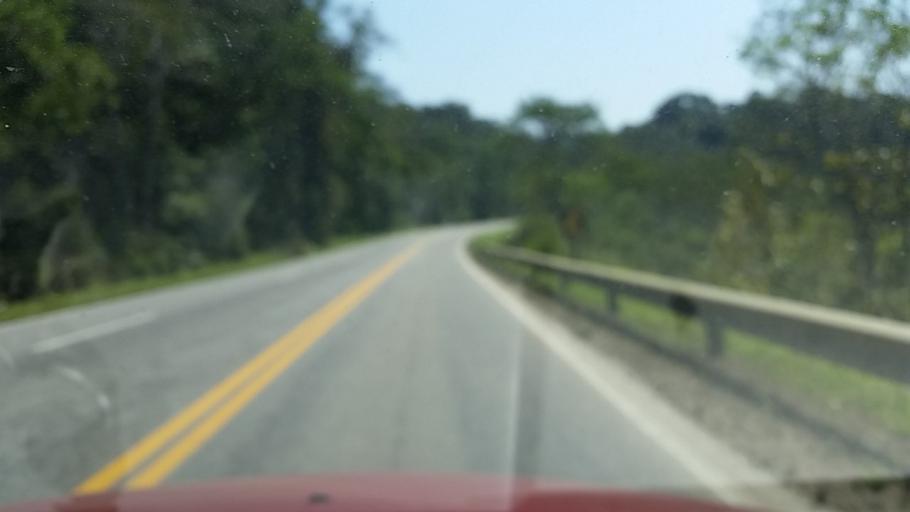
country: BR
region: Sao Paulo
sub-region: Miracatu
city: Miracatu
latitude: -24.3621
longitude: -47.4930
